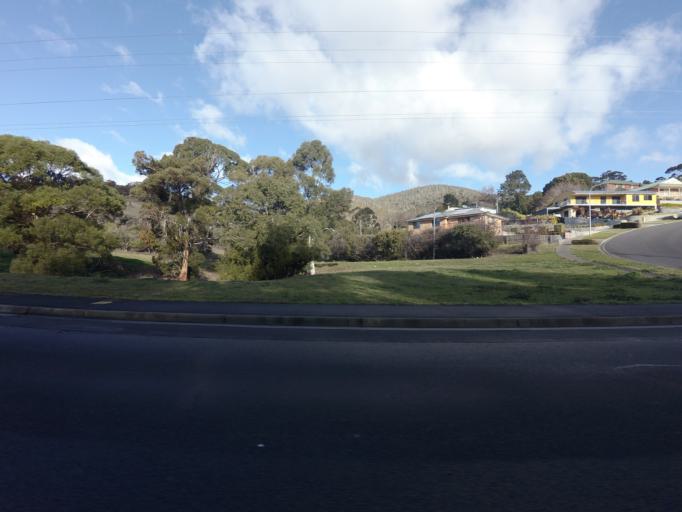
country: AU
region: Tasmania
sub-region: Glenorchy
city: Berriedale
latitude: -42.8139
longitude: 147.2358
